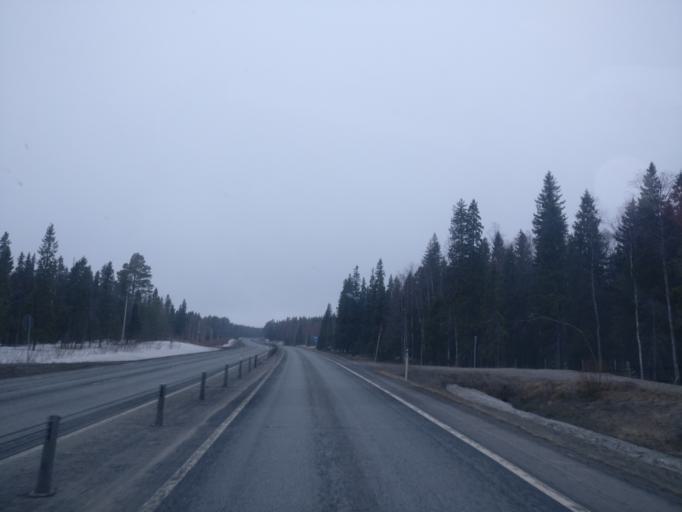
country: FI
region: Lapland
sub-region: Kemi-Tornio
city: Simo
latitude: 65.6689
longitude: 24.9555
